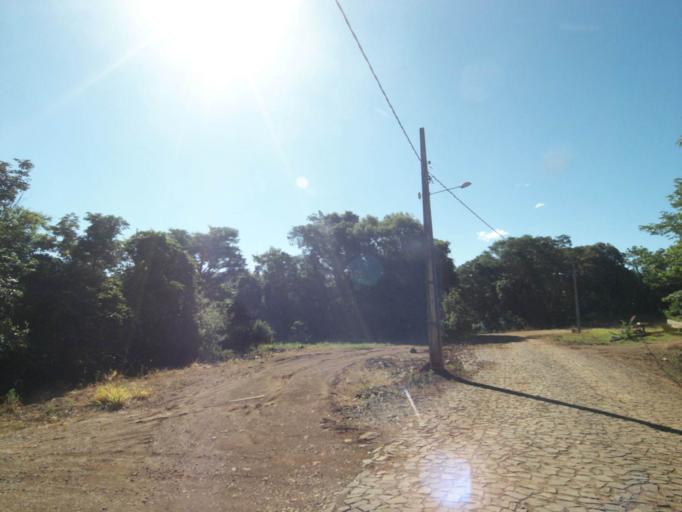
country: BR
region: Parana
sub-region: Ampere
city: Ampere
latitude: -26.1663
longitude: -53.3622
